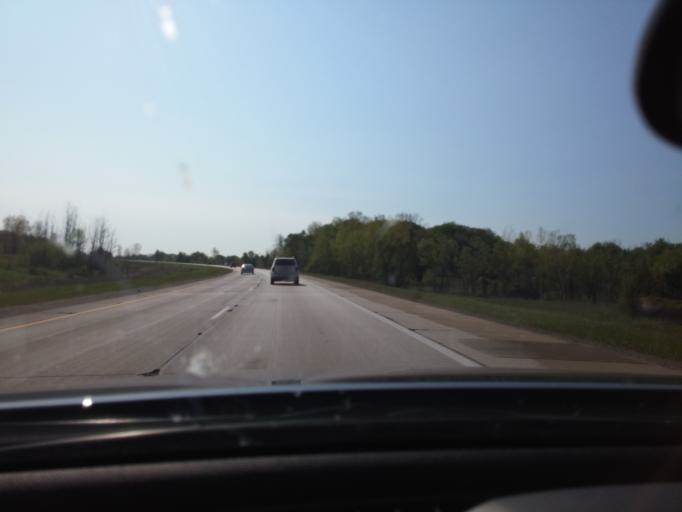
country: US
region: Michigan
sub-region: Lapeer County
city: Imlay City
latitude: 42.9975
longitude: -83.1415
